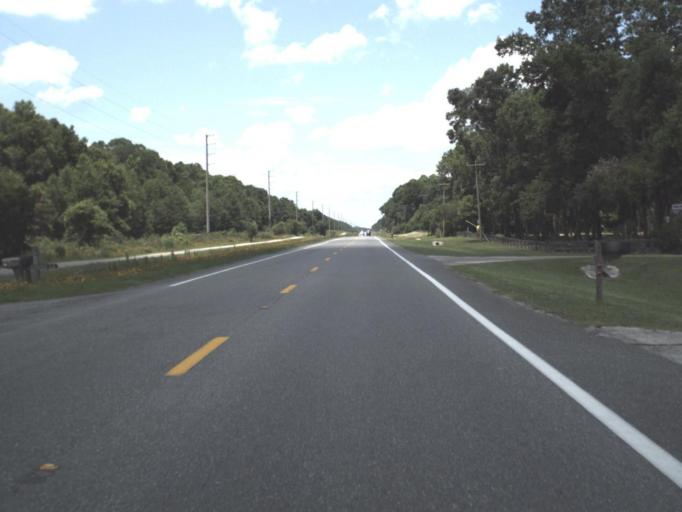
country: US
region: Florida
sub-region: Alachua County
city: High Springs
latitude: 29.9533
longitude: -82.7973
